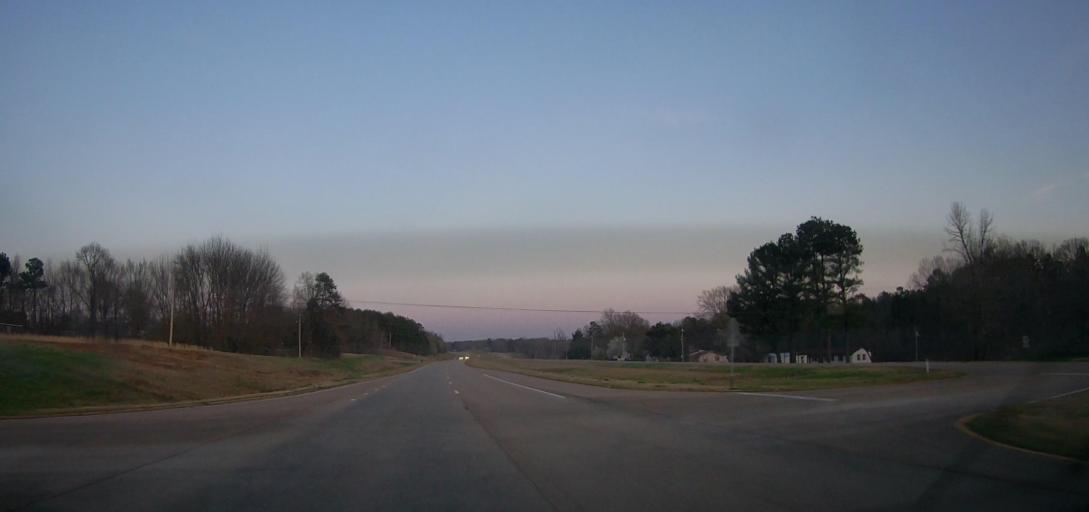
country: US
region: Mississippi
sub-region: Tippah County
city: Ripley
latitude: 34.9533
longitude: -88.8359
